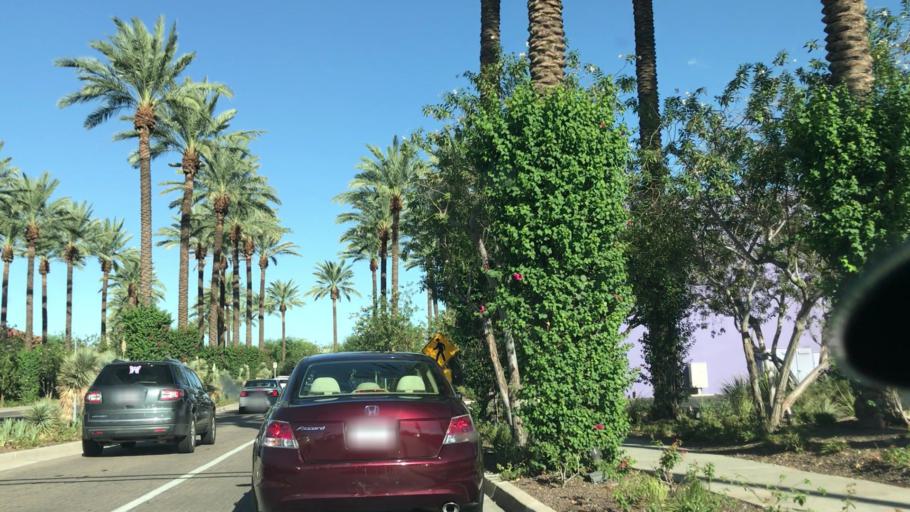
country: US
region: Arizona
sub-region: Maricopa County
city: Tempe
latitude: 33.4320
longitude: -111.9090
